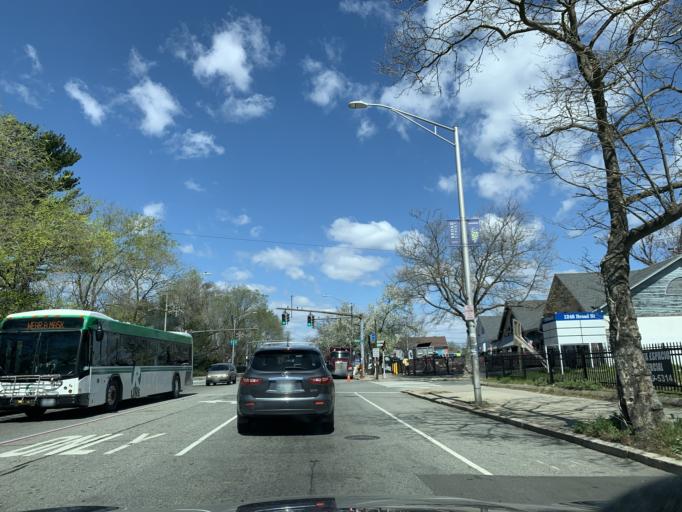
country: US
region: Rhode Island
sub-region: Providence County
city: Providence
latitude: 41.7924
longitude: -71.4075
